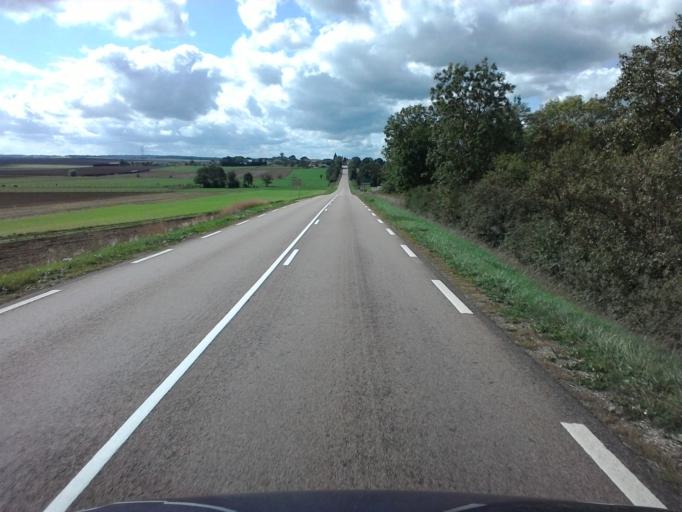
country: FR
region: Lorraine
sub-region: Departement de Meurthe-et-Moselle
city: Colombey-les-Belles
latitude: 48.4909
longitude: 5.8599
